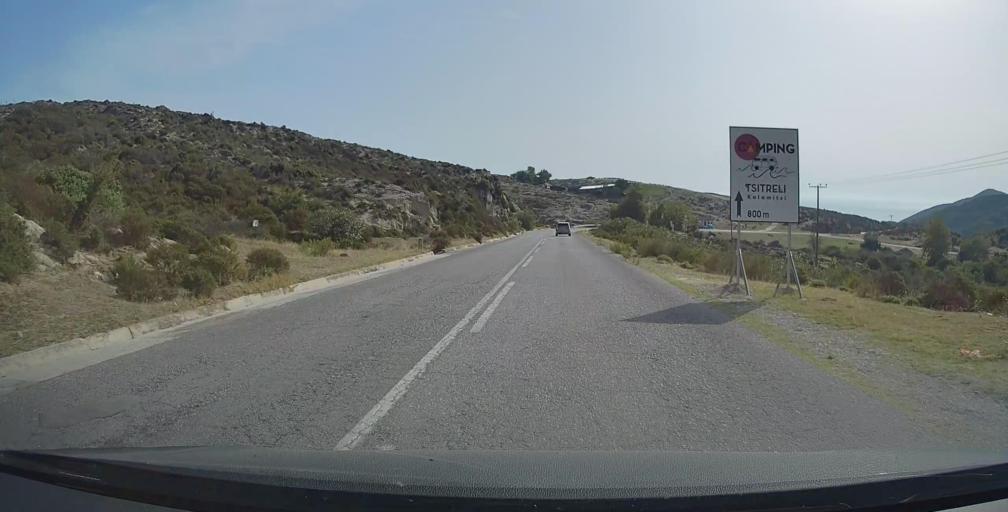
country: GR
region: Central Macedonia
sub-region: Nomos Chalkidikis
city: Sykia
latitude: 39.9904
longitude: 23.9669
